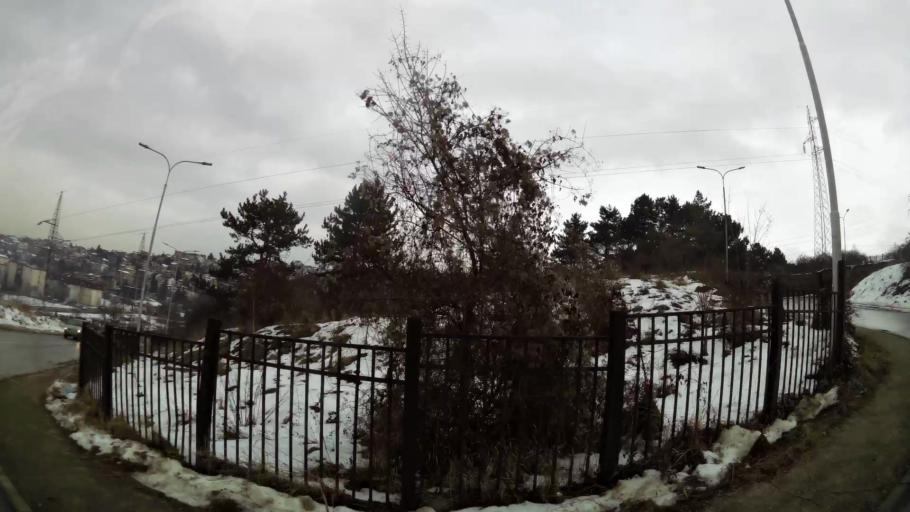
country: XK
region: Pristina
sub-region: Komuna e Prishtines
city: Pristina
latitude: 42.6637
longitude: 21.1783
